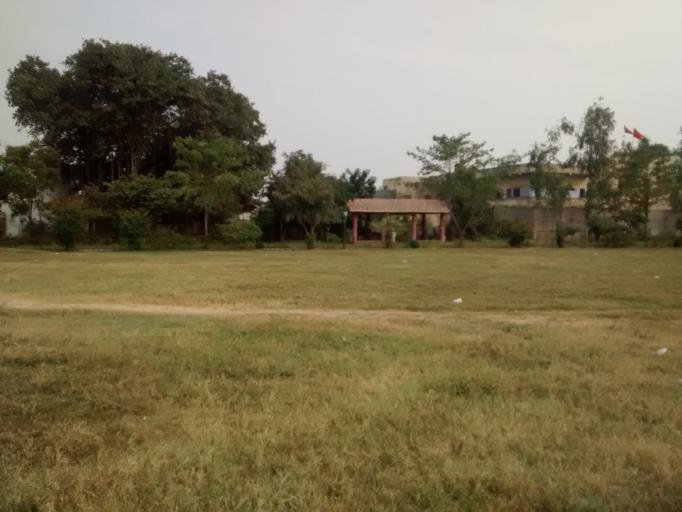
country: IN
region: Gujarat
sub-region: Gandhinagar
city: Dahegam
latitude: 23.1682
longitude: 72.8193
